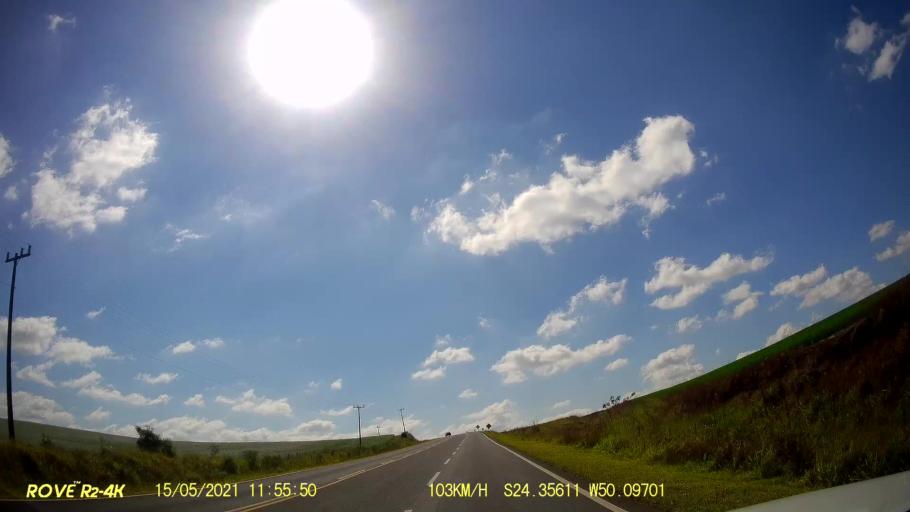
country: BR
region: Parana
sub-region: Pirai Do Sul
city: Pirai do Sul
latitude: -24.3563
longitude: -50.0980
